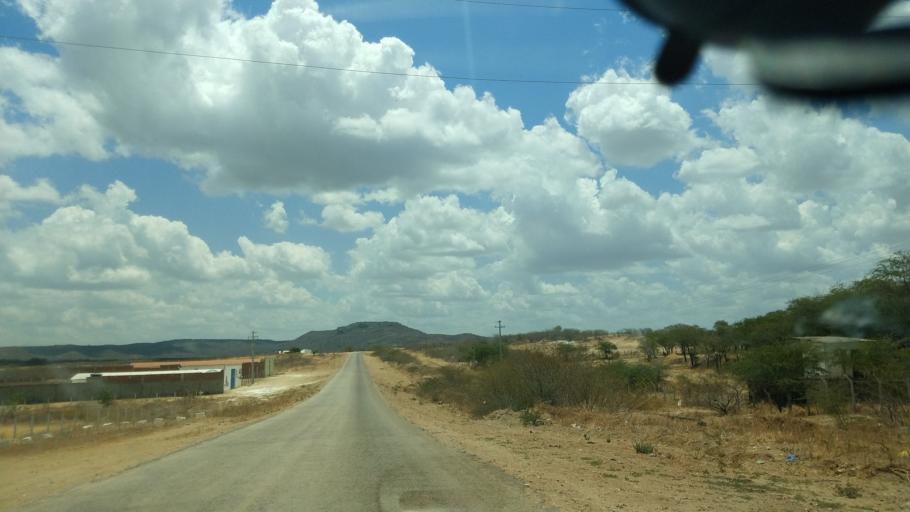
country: BR
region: Rio Grande do Norte
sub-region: Currais Novos
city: Currais Novos
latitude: -6.2779
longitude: -36.5330
